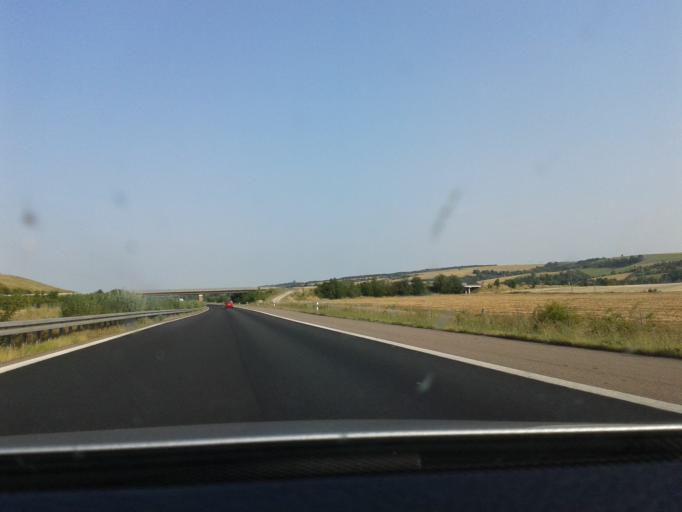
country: DE
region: Saxony-Anhalt
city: Bennungen
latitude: 51.4653
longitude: 11.1295
